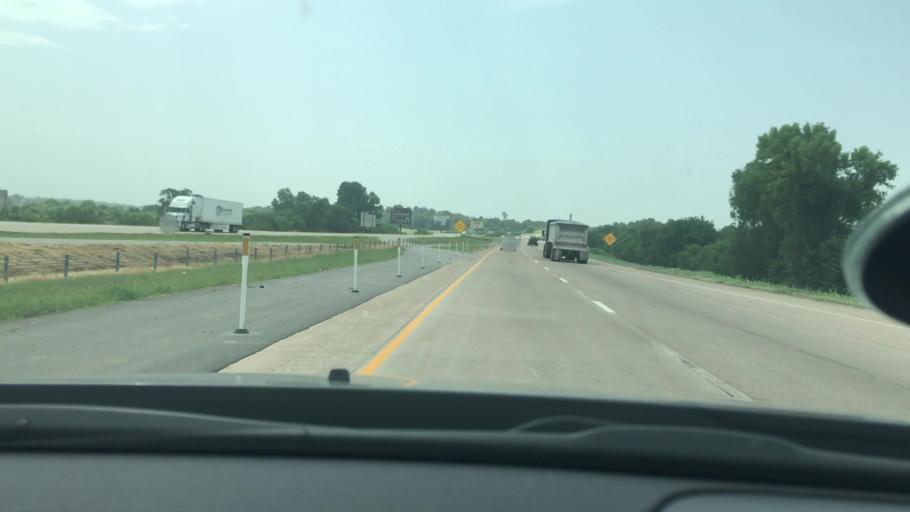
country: US
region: Oklahoma
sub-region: Garvin County
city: Pauls Valley
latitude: 34.7353
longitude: -97.2600
